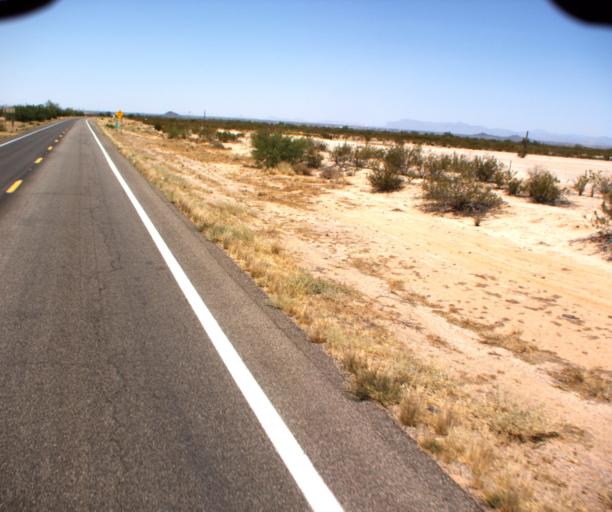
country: US
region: Arizona
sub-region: Pinal County
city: Florence
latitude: 32.9844
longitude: -111.3583
